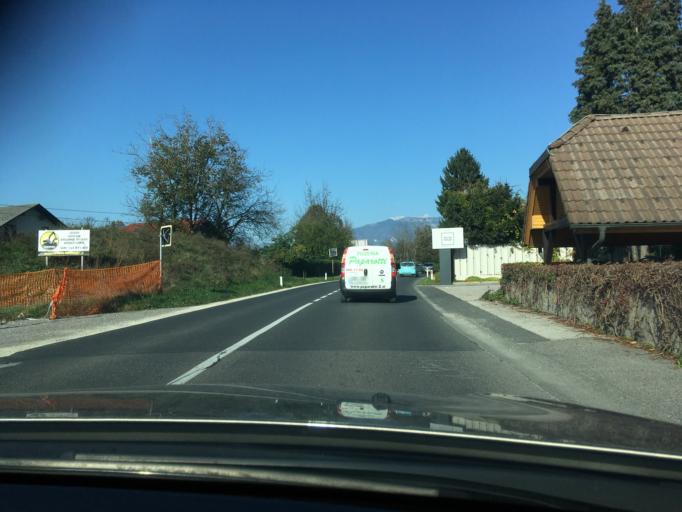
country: SI
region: Domzale
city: Domzale
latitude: 46.1466
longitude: 14.5929
